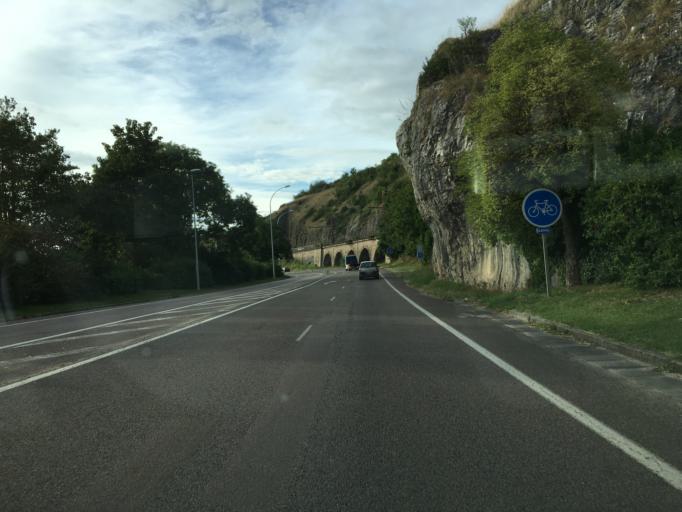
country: FR
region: Bourgogne
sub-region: Departement de la Cote-d'Or
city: Talant
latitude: 47.3260
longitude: 5.0074
